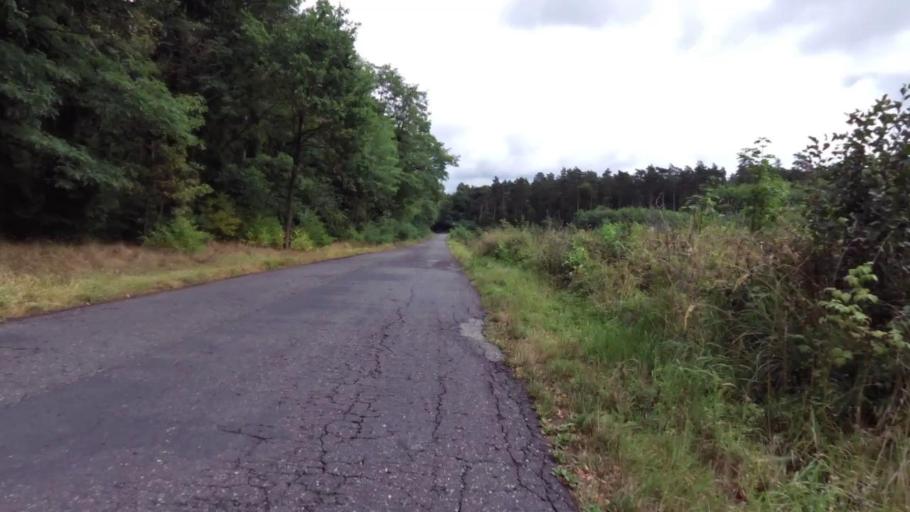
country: PL
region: West Pomeranian Voivodeship
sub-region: Powiat mysliborski
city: Debno
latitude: 52.8501
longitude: 14.6878
